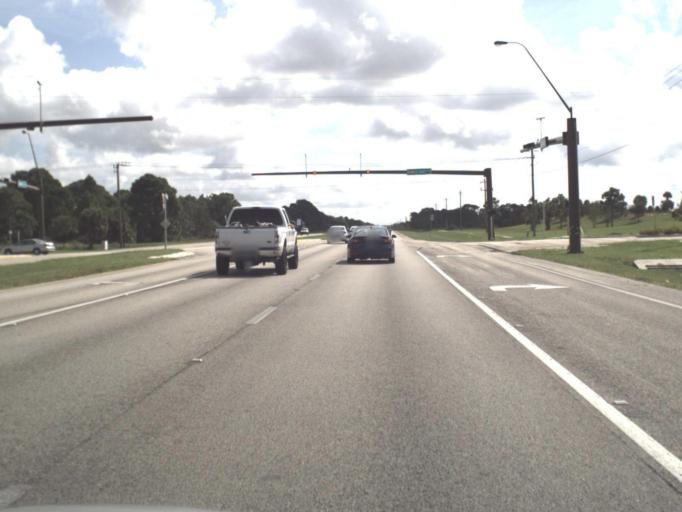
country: US
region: Florida
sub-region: Sarasota County
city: Plantation
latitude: 27.0496
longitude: -82.3783
